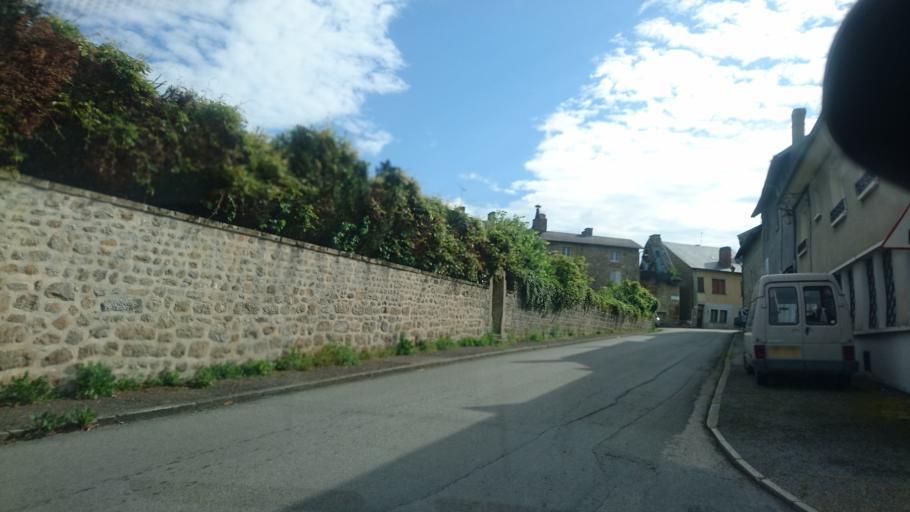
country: FR
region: Limousin
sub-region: Departement de la Haute-Vienne
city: Peyrat-le-Chateau
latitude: 45.8142
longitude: 1.7734
